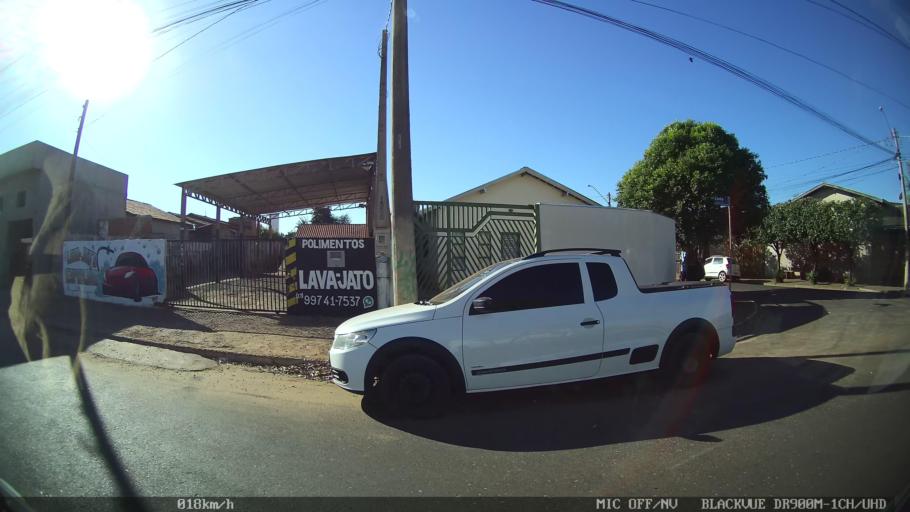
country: BR
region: Sao Paulo
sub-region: Olimpia
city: Olimpia
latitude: -20.7267
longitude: -48.9017
